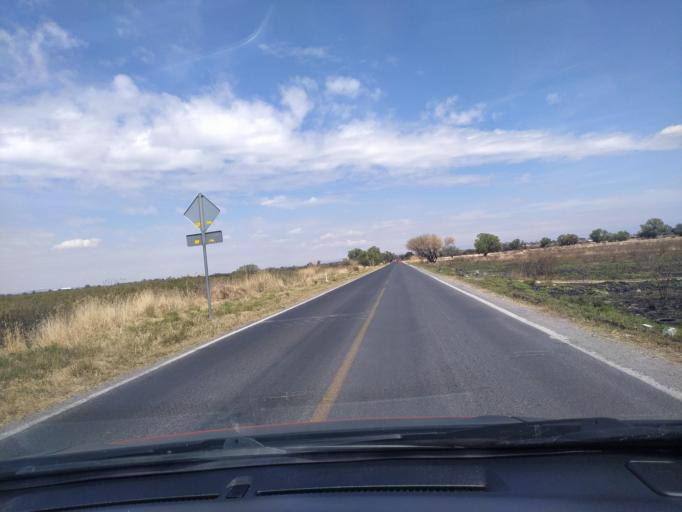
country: MX
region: Guanajuato
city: San Roque
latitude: 20.9489
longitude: -101.8533
